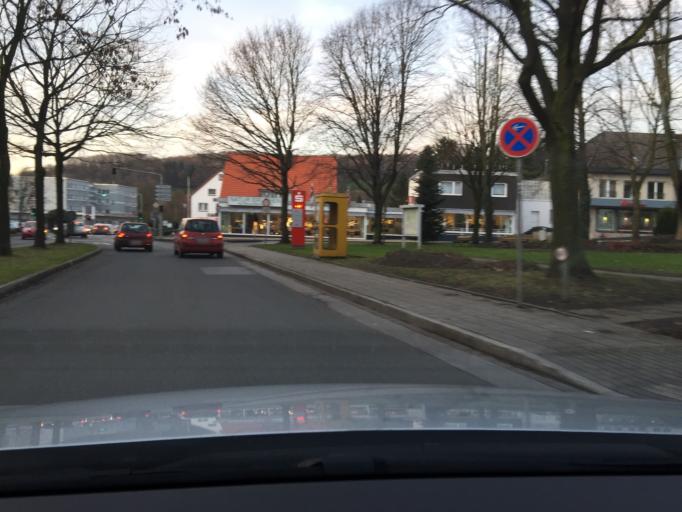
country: DE
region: North Rhine-Westphalia
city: Hattingen
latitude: 51.3726
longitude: 7.1374
